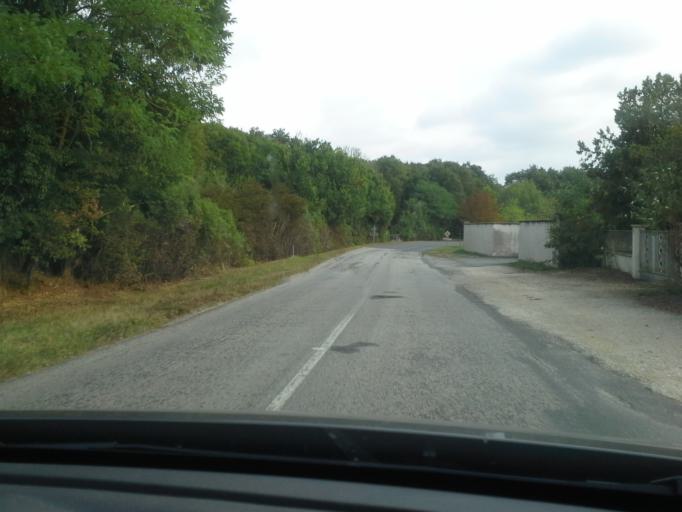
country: FR
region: Centre
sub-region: Departement du Loir-et-Cher
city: Herbault
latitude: 47.5871
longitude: 1.2010
